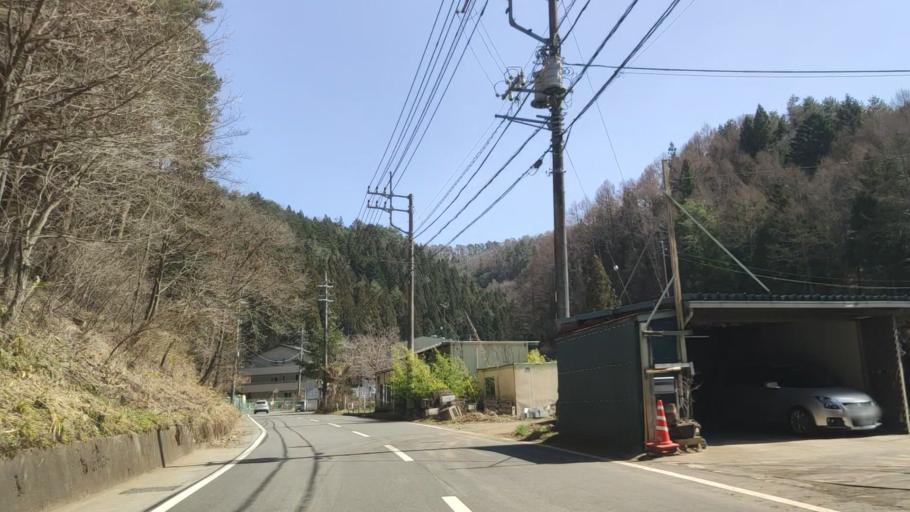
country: JP
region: Yamanashi
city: Fujikawaguchiko
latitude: 35.4631
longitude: 138.8172
